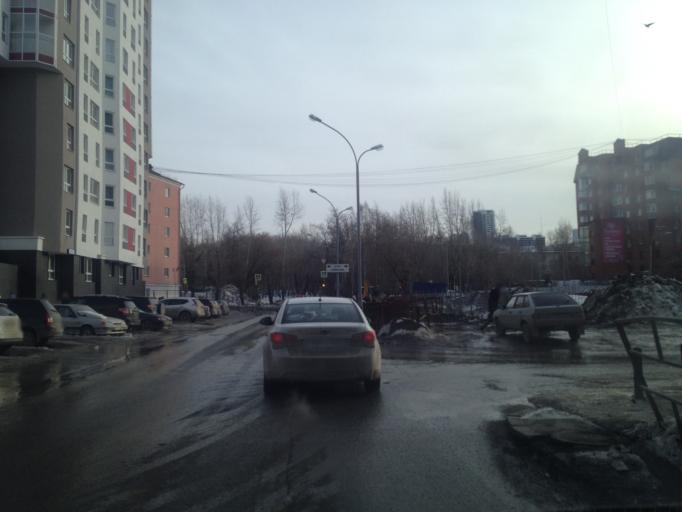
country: RU
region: Sverdlovsk
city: Yekaterinburg
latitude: 56.8429
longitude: 60.5733
